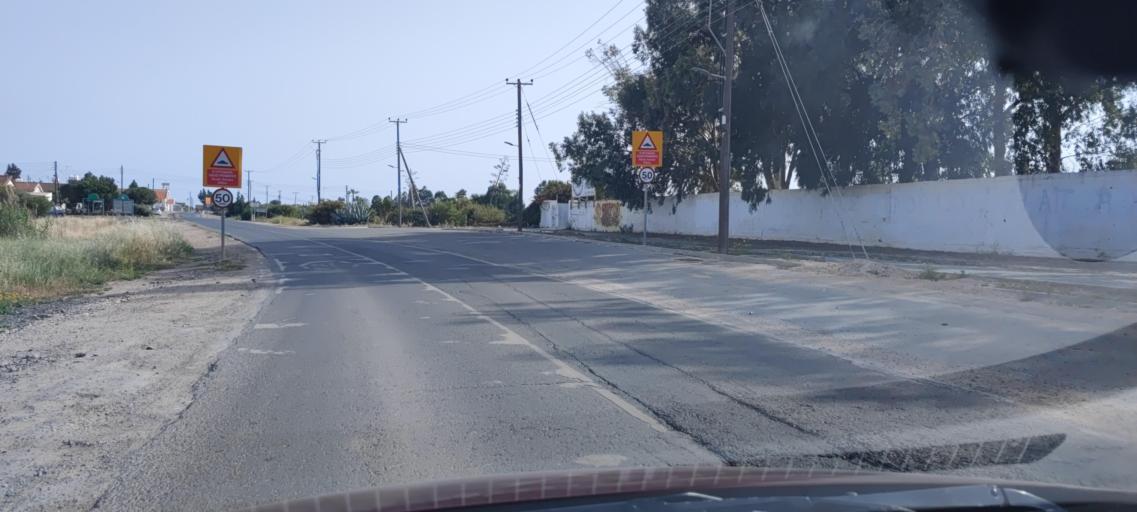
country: CY
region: Ammochostos
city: Deryneia
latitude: 35.0530
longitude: 33.9573
